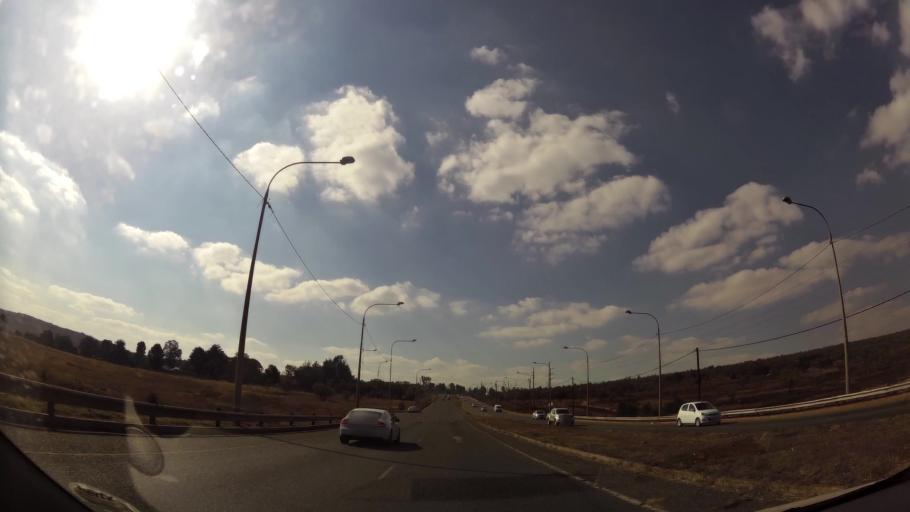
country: ZA
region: Gauteng
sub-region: West Rand District Municipality
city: Krugersdorp
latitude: -26.0682
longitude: 27.8035
